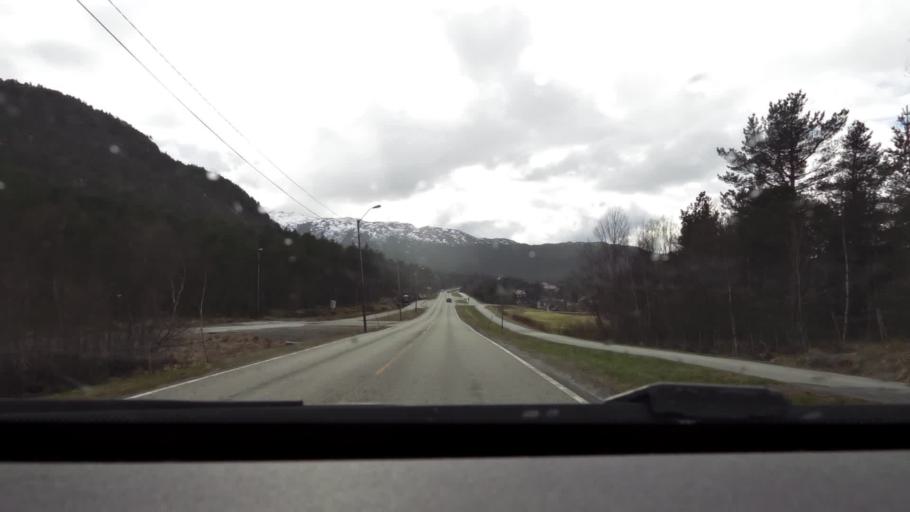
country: NO
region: More og Romsdal
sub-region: Kristiansund
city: Rensvik
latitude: 63.0869
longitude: 7.7975
